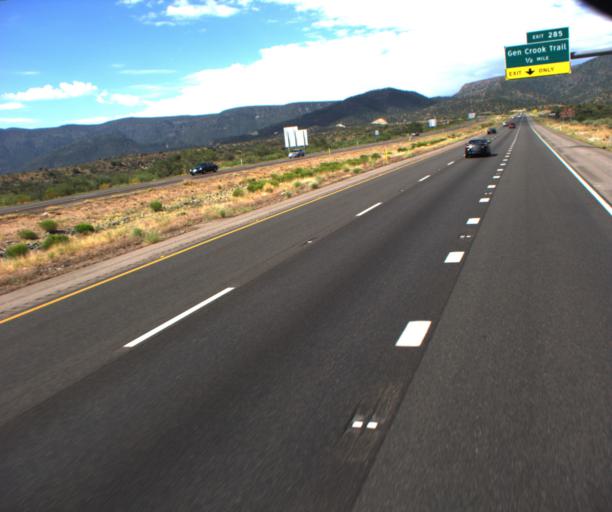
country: US
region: Arizona
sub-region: Yavapai County
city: Camp Verde
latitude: 34.5703
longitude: -111.8927
